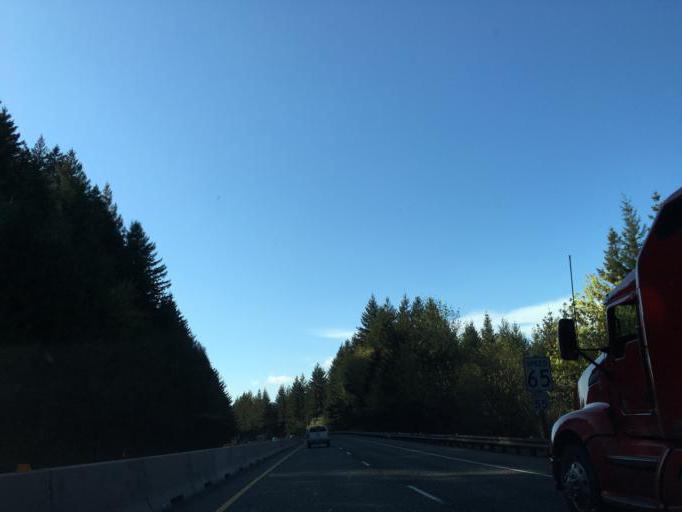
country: US
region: Washington
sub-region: Skamania County
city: Carson
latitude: 45.6912
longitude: -121.7821
